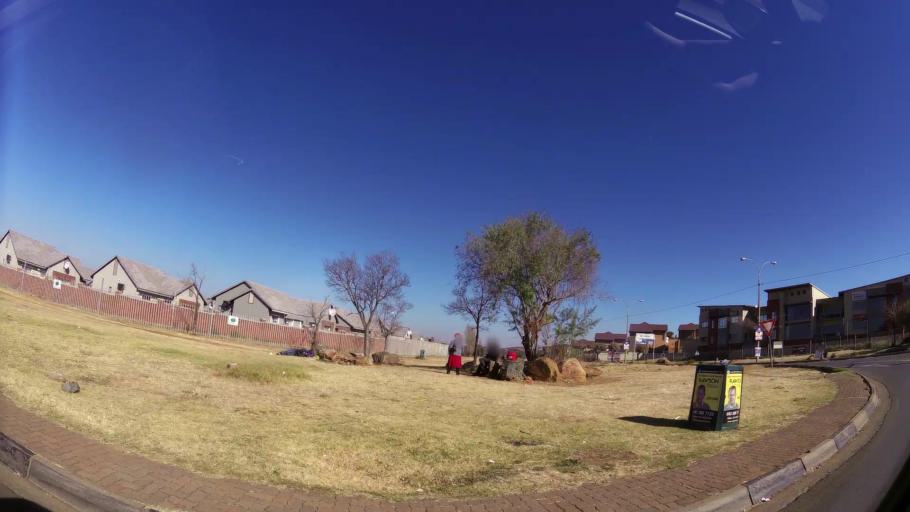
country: ZA
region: Gauteng
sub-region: City of Johannesburg Metropolitan Municipality
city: Johannesburg
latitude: -26.2899
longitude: 28.0899
